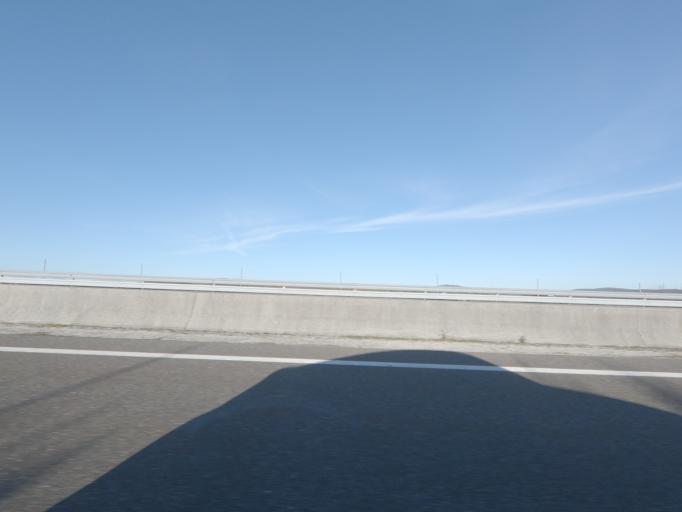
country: ES
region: Galicia
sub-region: Provincia de Pontevedra
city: Dozon
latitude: 42.5543
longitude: -8.0198
